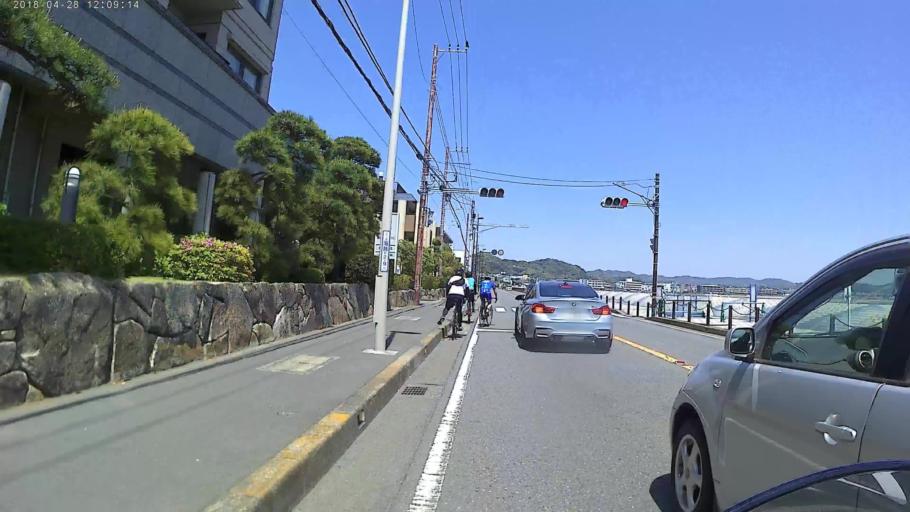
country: JP
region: Kanagawa
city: Kamakura
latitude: 35.3050
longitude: 139.5322
